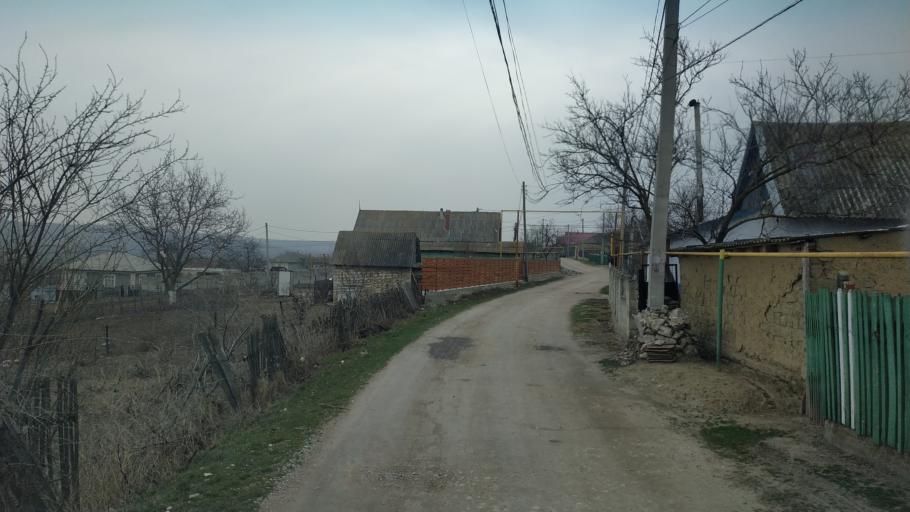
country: MD
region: Chisinau
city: Singera
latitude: 46.8266
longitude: 29.0311
